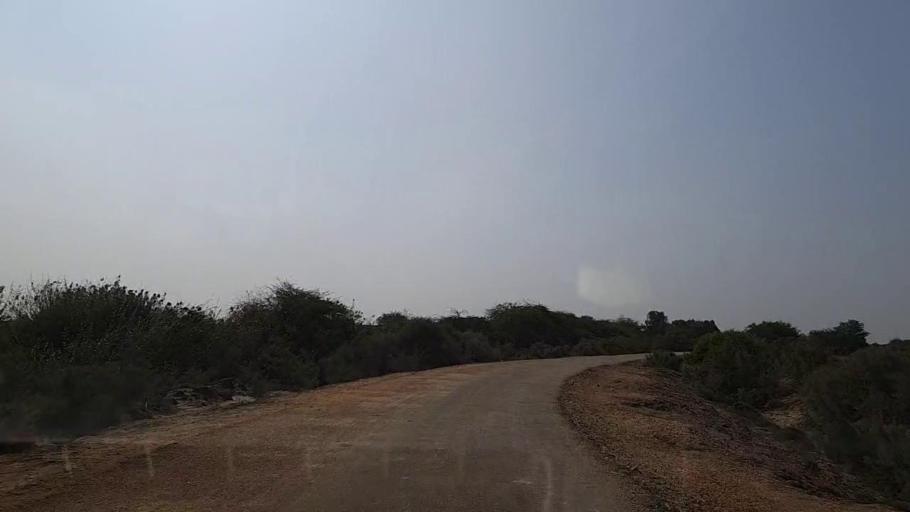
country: PK
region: Sindh
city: Mirpur Sakro
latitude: 24.5257
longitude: 67.7743
